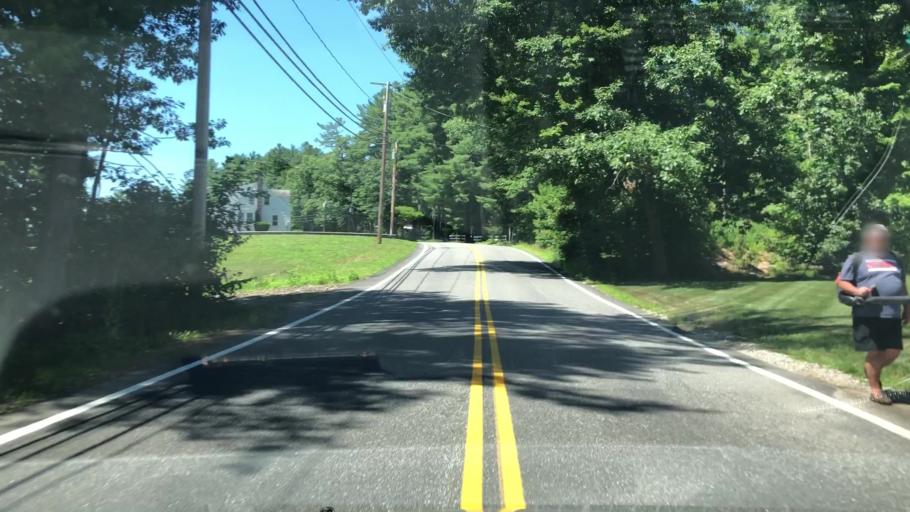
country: US
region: New Hampshire
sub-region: Hillsborough County
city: Milford
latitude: 42.8385
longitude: -71.6054
